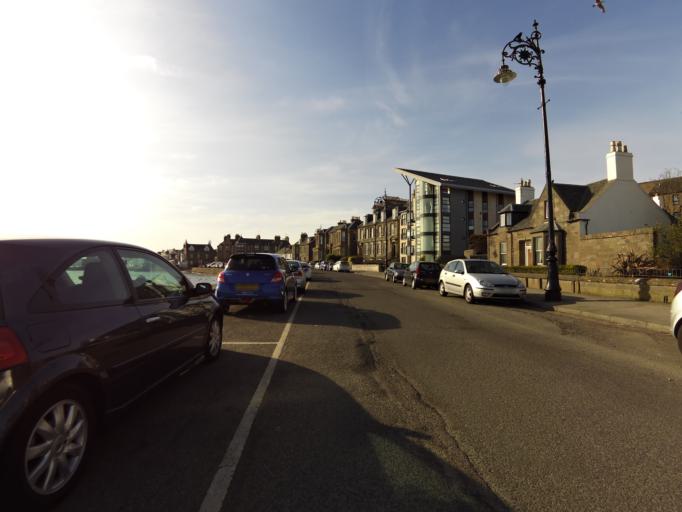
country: GB
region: Scotland
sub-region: Fife
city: Tayport
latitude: 56.4643
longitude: -2.8722
